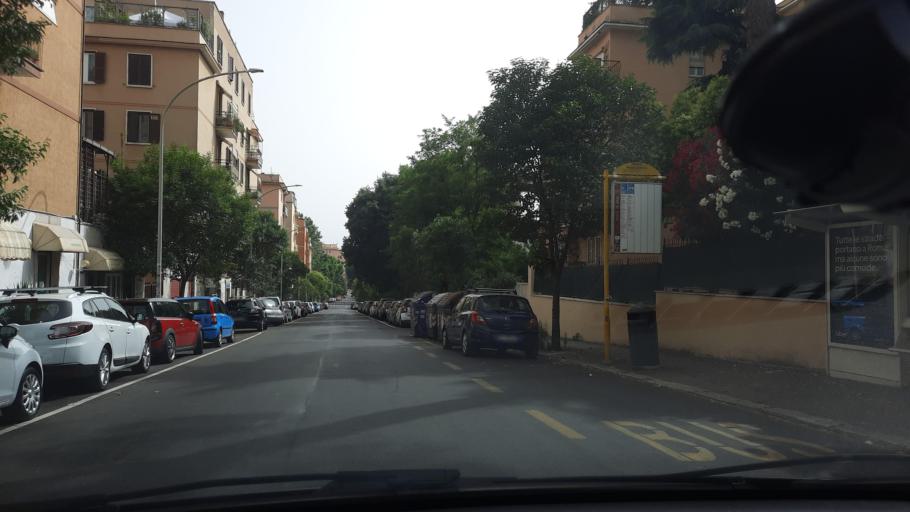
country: IT
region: Latium
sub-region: Citta metropolitana di Roma Capitale
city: Rome
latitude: 41.8583
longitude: 12.4894
